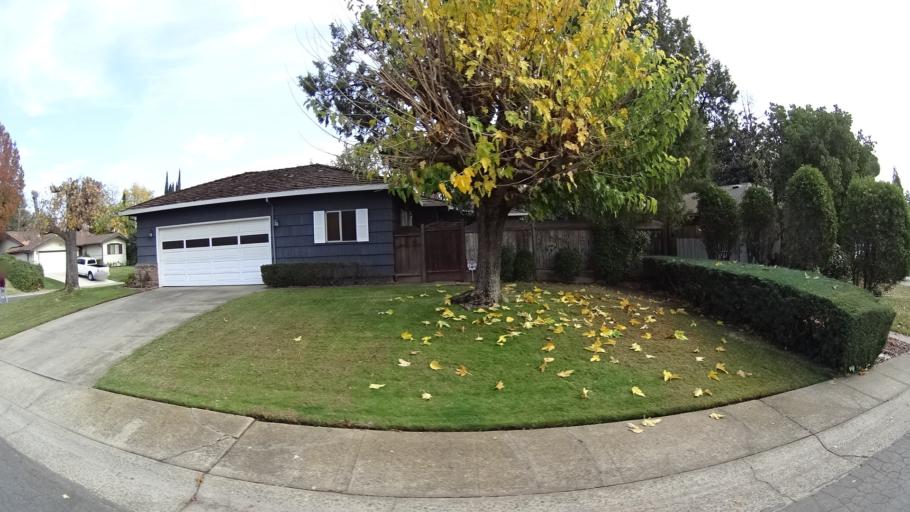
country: US
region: California
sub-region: Sacramento County
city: Fair Oaks
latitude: 38.6704
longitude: -121.2802
